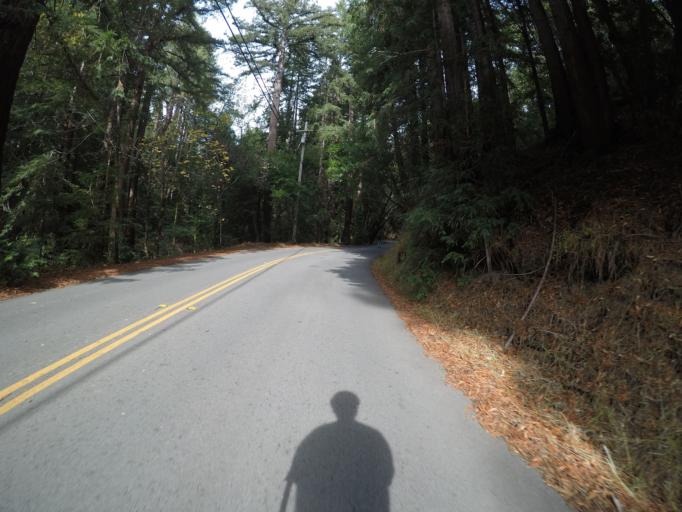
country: US
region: California
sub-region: Santa Cruz County
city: Scotts Valley
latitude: 37.0264
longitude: -121.9959
